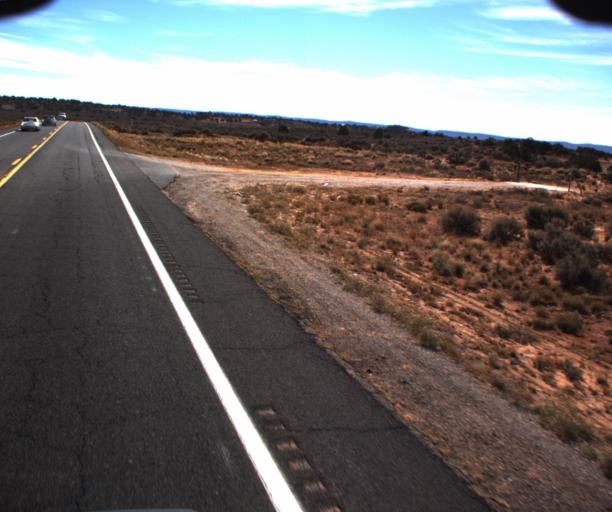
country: US
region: Arizona
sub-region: Coconino County
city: Kaibito
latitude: 36.5531
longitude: -110.7058
